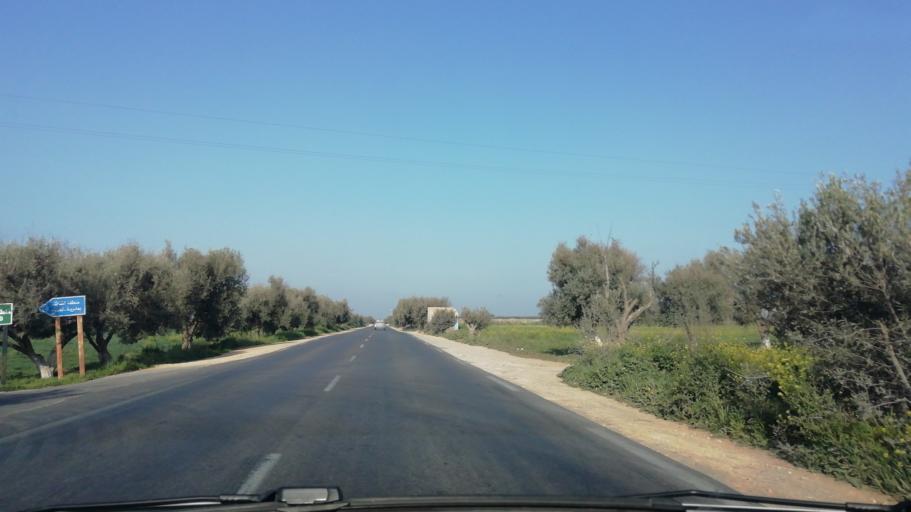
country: DZ
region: Mostaganem
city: Mostaganem
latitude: 35.7483
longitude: 0.1328
